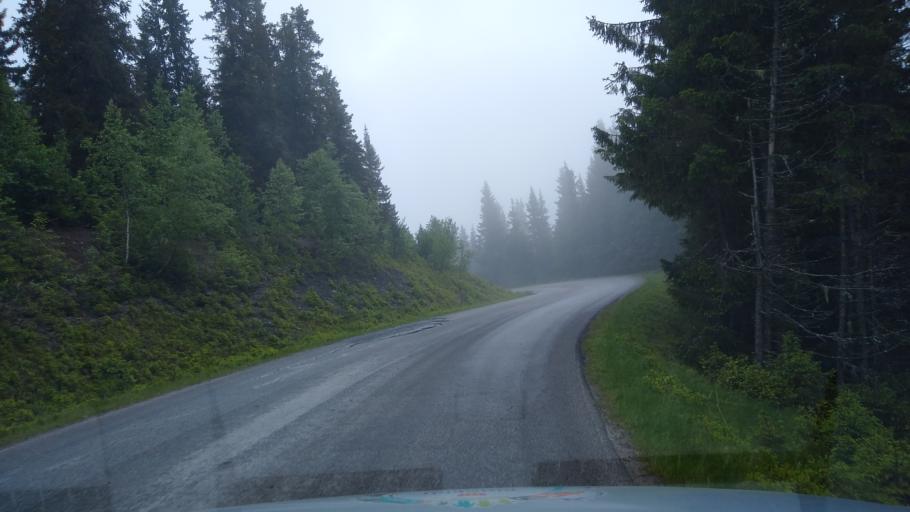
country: NO
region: Oppland
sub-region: Ringebu
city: Ringebu
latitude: 61.4928
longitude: 10.1214
